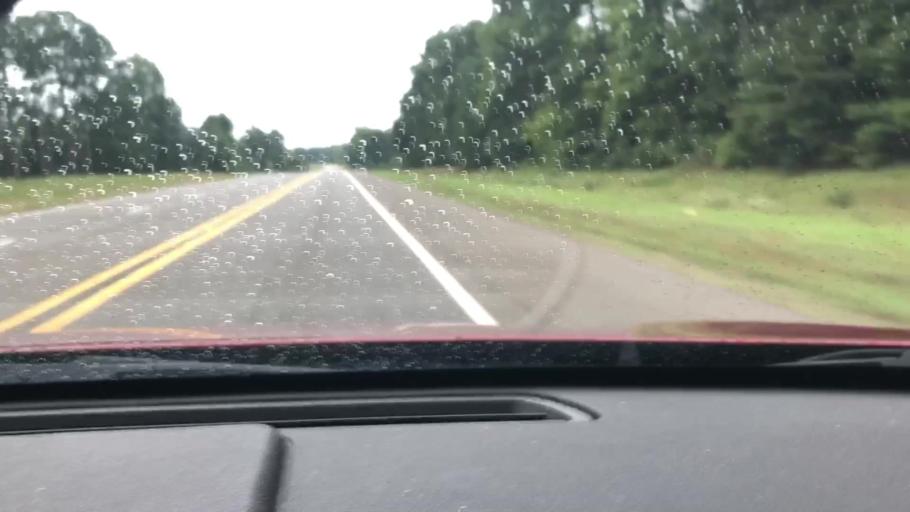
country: US
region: Arkansas
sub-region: Lafayette County
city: Stamps
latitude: 33.3632
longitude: -93.4664
